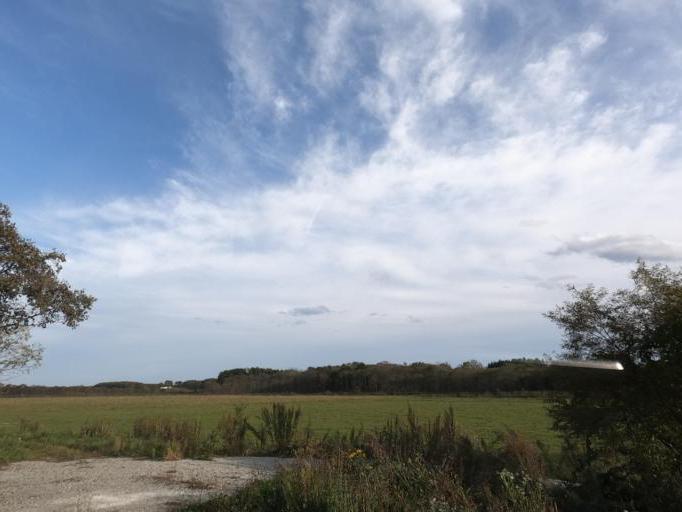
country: JP
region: Hokkaido
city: Obihiro
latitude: 42.5042
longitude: 143.4175
